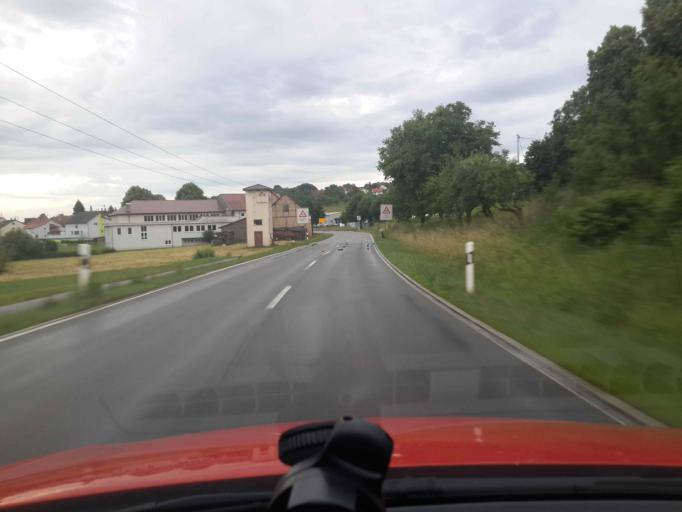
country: DE
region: Baden-Wuerttemberg
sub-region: Karlsruhe Region
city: Billigheim
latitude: 49.3554
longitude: 9.2162
